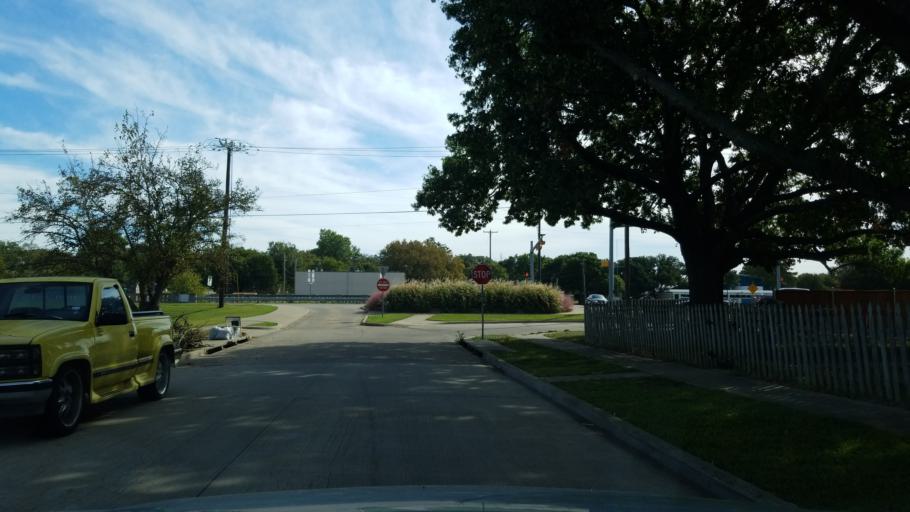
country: US
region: Texas
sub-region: Dallas County
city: Garland
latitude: 32.9071
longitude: -96.6492
